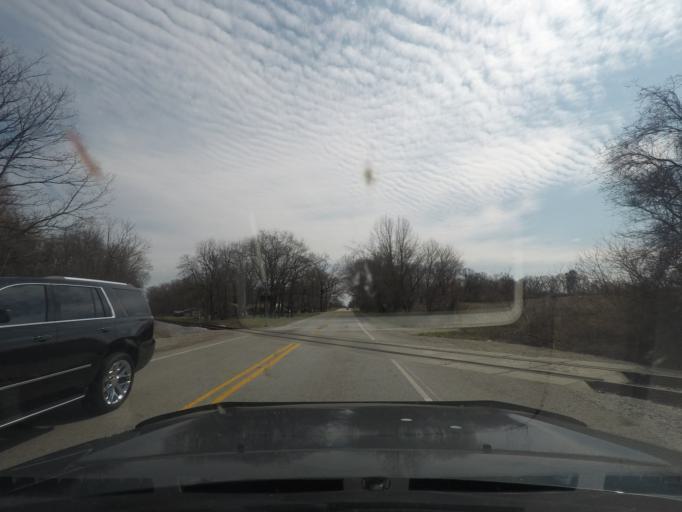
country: US
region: Indiana
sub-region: LaPorte County
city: Trail Creek
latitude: 41.6799
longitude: -86.7884
